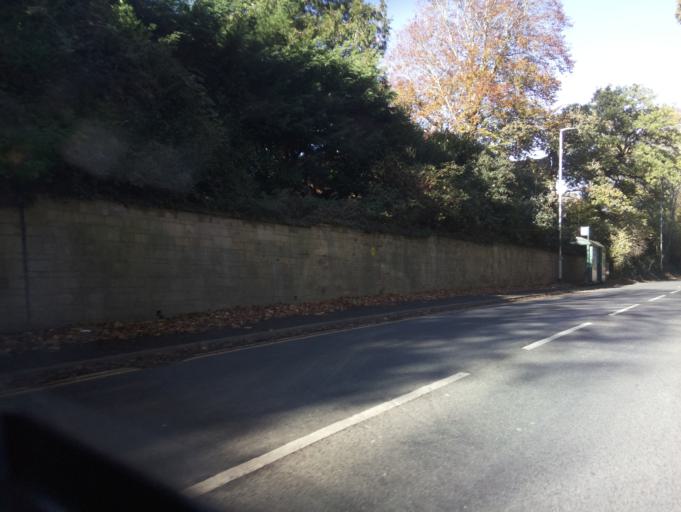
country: GB
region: England
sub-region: Somerset
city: Yeovil
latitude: 50.9484
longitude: -2.6392
